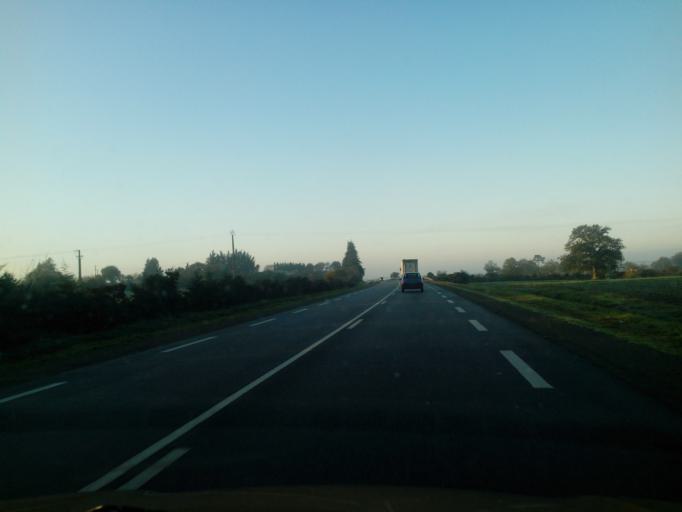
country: FR
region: Brittany
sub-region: Departement du Morbihan
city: Loyat
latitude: 48.0087
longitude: -2.3478
